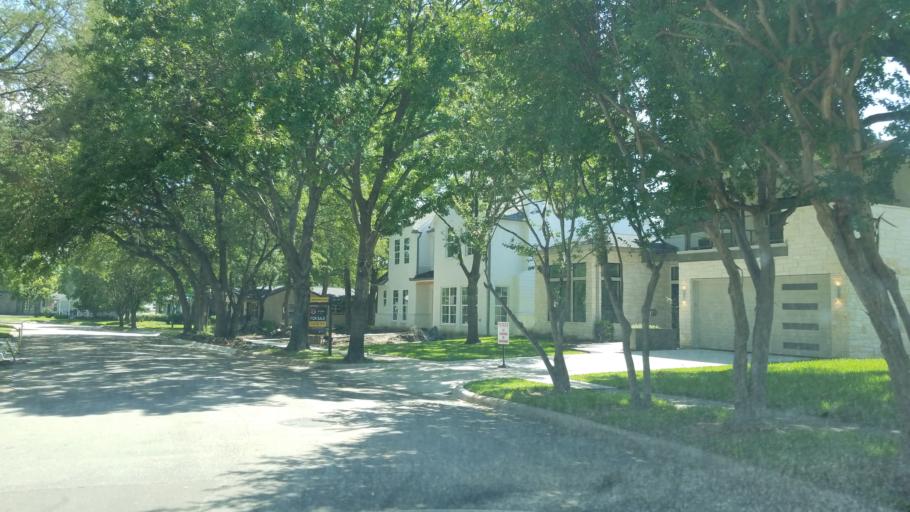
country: US
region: Texas
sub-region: Dallas County
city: University Park
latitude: 32.8782
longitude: -96.8513
